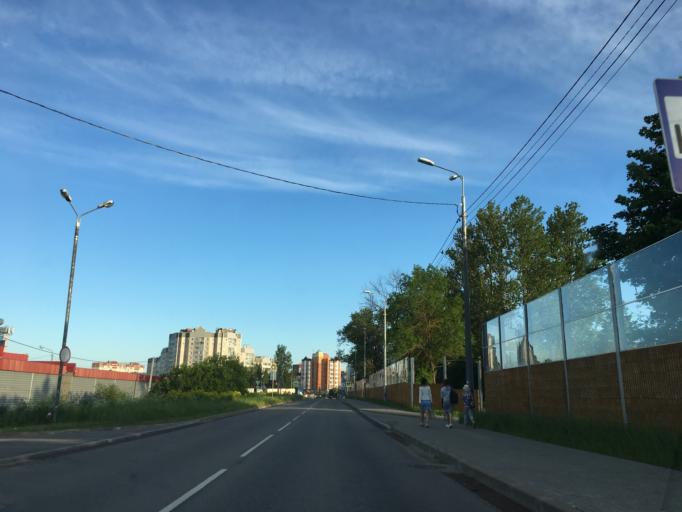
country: RU
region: Leningrad
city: Gatchina
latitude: 59.5830
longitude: 30.1369
